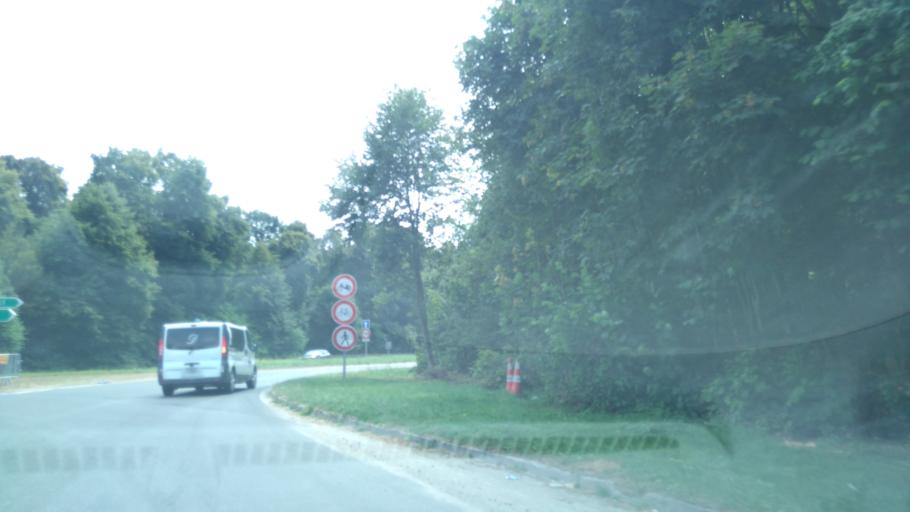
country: FR
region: Picardie
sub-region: Departement de l'Oise
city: Saint-Maximin
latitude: 49.2209
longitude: 2.4667
